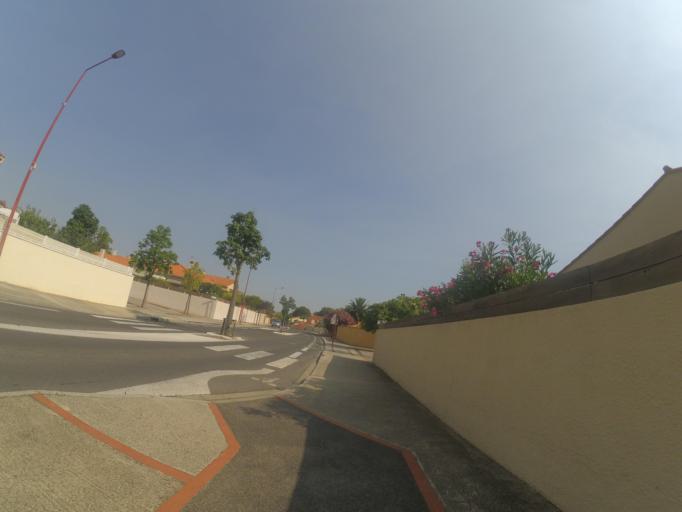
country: FR
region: Languedoc-Roussillon
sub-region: Departement des Pyrenees-Orientales
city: Toulouges
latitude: 42.6690
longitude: 2.8354
